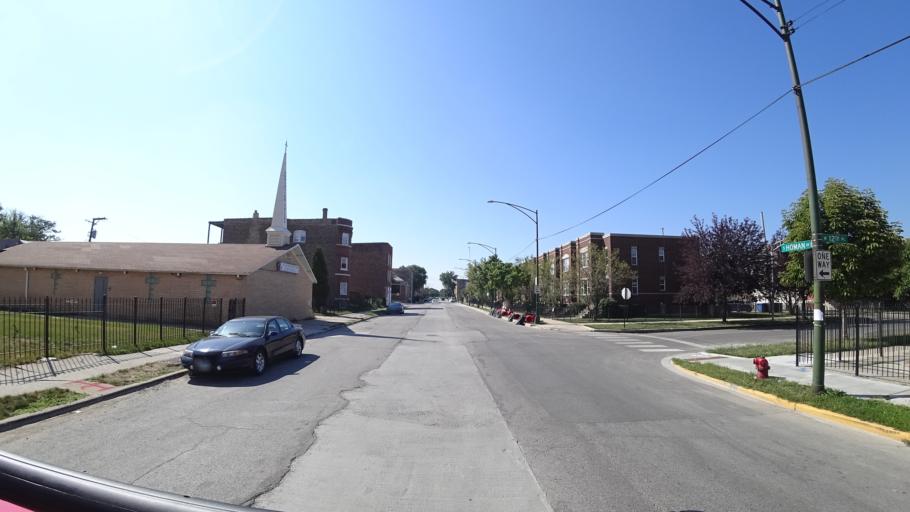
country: US
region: Illinois
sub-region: Cook County
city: Cicero
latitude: 41.8653
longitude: -87.7105
